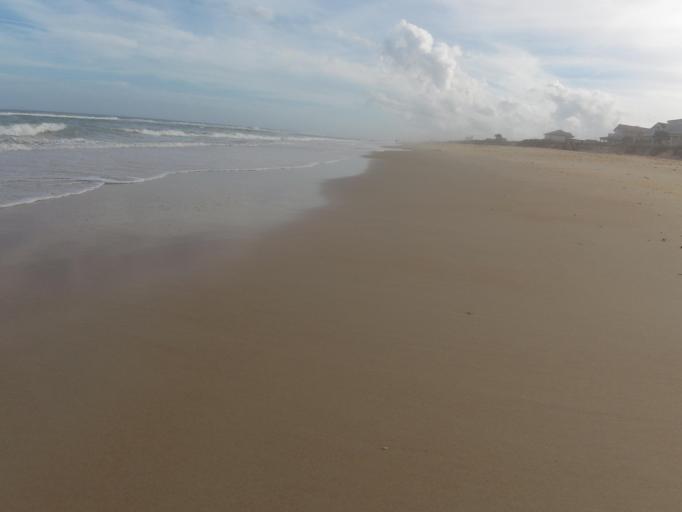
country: US
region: Florida
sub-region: Flagler County
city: Palm Coast
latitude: 29.6233
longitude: -81.1931
